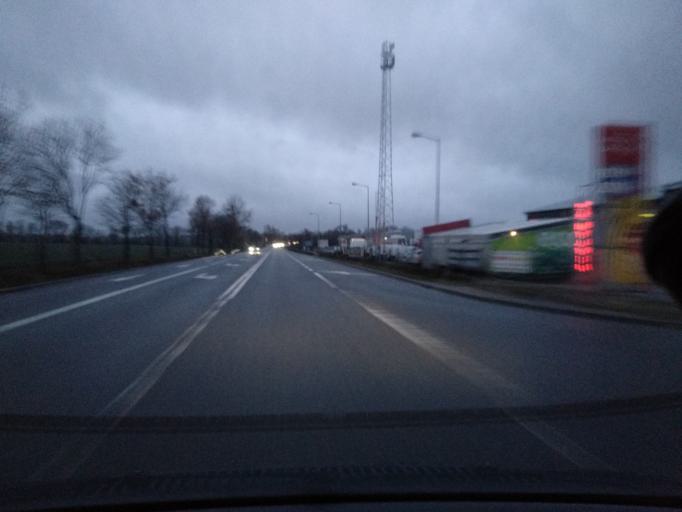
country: PL
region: Lower Silesian Voivodeship
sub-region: Powiat sredzki
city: Sroda Slaska
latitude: 51.1643
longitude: 16.6277
